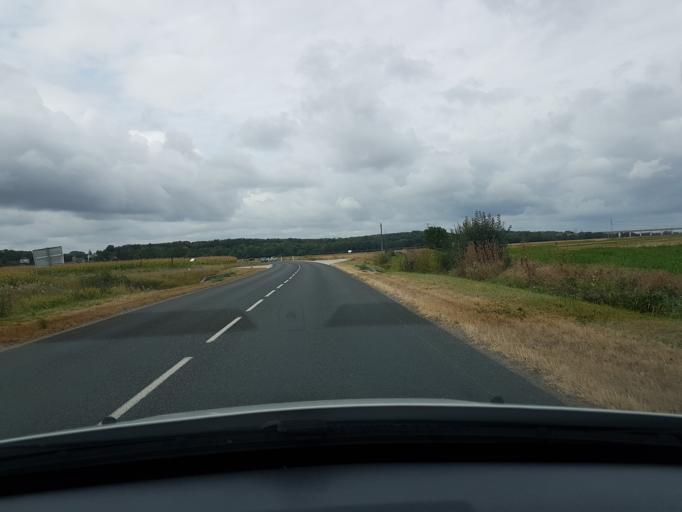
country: FR
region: Centre
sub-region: Departement d'Indre-et-Loire
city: Veretz
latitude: 47.3681
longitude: 0.8152
